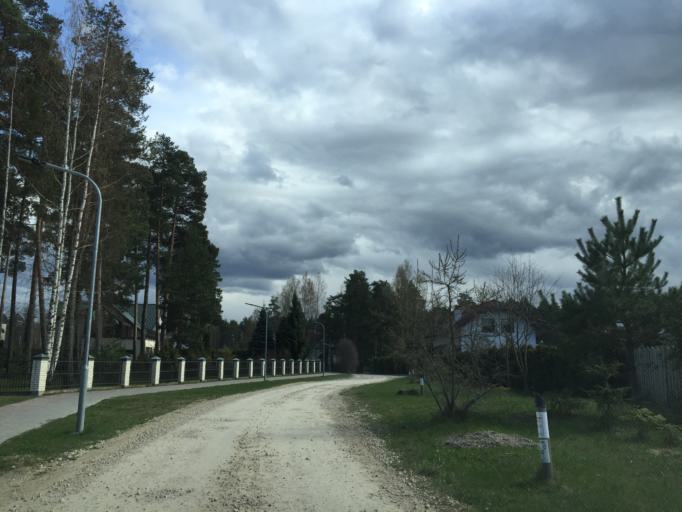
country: LV
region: Riga
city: Bergi
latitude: 56.9888
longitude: 24.3080
